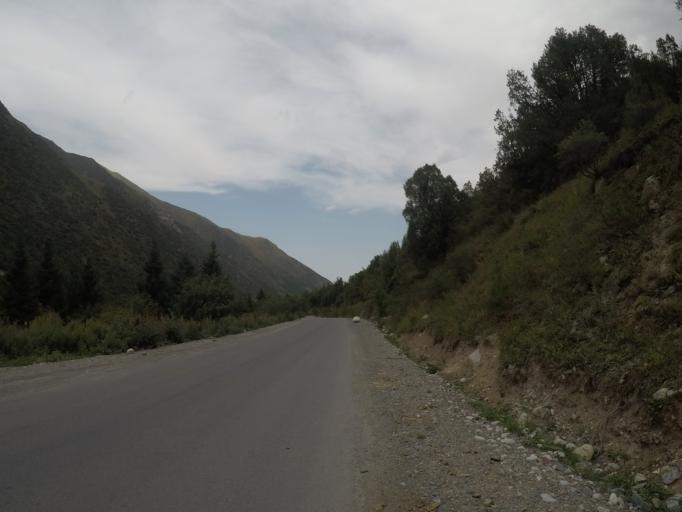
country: KG
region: Chuy
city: Bishkek
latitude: 42.5874
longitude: 74.4841
